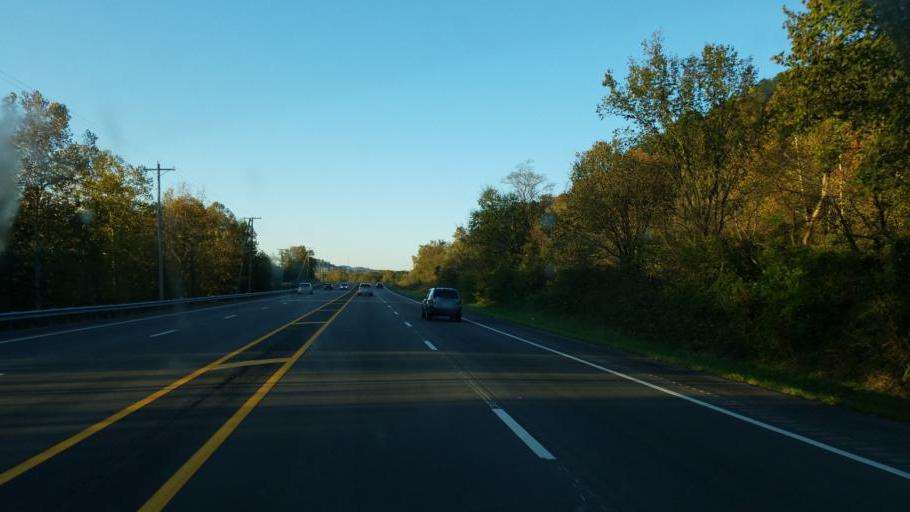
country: US
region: Ohio
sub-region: Scioto County
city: Lucasville
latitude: 38.8476
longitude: -82.9864
